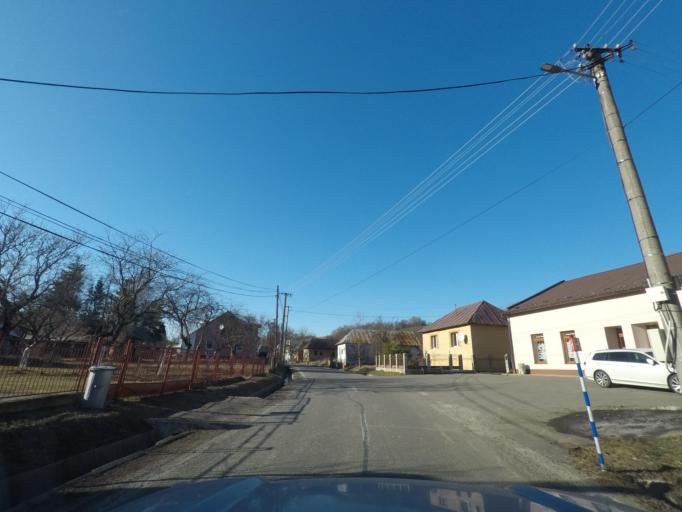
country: SK
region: Presovsky
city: Medzilaborce
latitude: 49.1943
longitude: 22.0025
